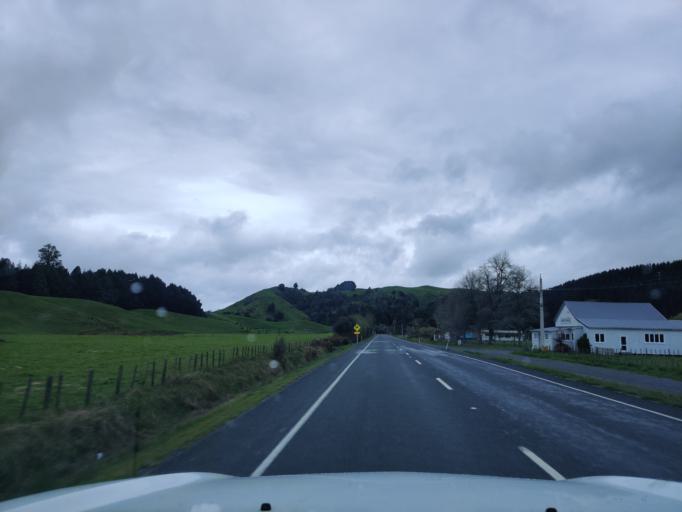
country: NZ
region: Waikato
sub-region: Otorohanga District
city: Otorohanga
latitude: -38.5784
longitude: 175.2150
